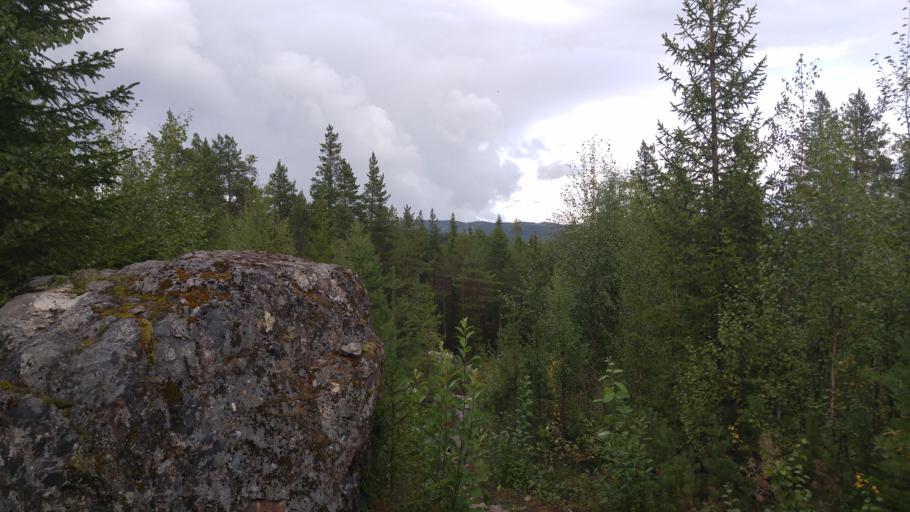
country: NO
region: Buskerud
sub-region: Gol
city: Gol
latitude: 60.6346
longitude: 9.0086
